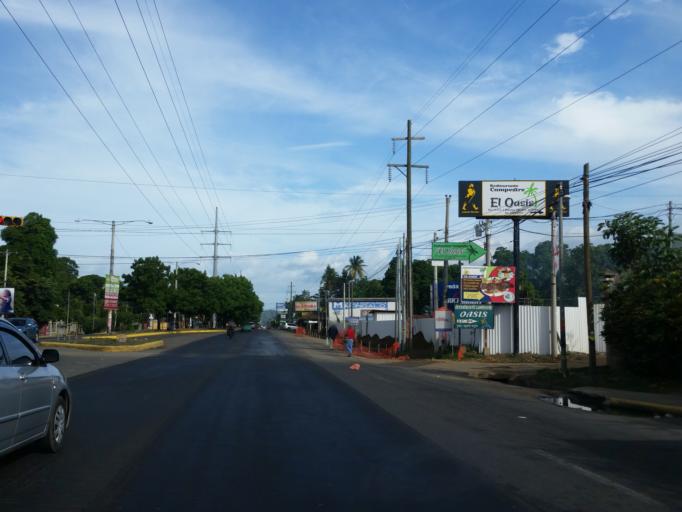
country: NI
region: Masaya
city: Ticuantepe
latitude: 12.0744
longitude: -86.2201
